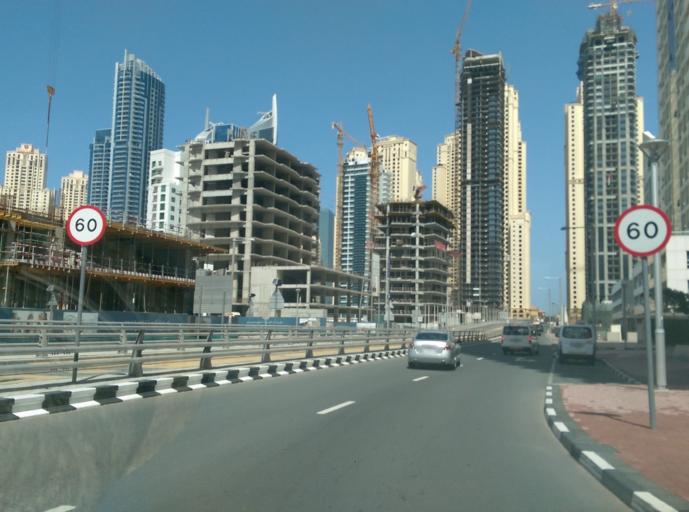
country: AE
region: Dubai
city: Dubai
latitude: 25.0783
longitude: 55.1431
